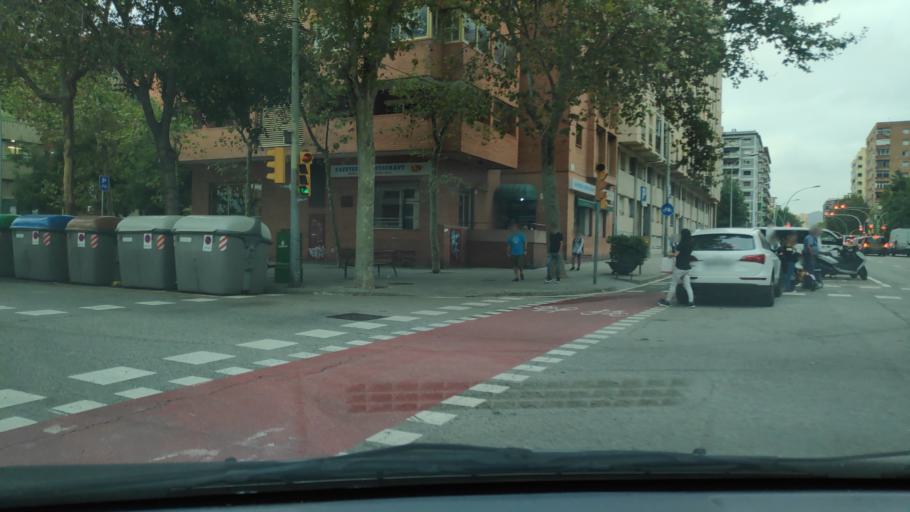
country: ES
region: Catalonia
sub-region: Provincia de Barcelona
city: Sant Marti
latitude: 41.4160
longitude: 2.2063
